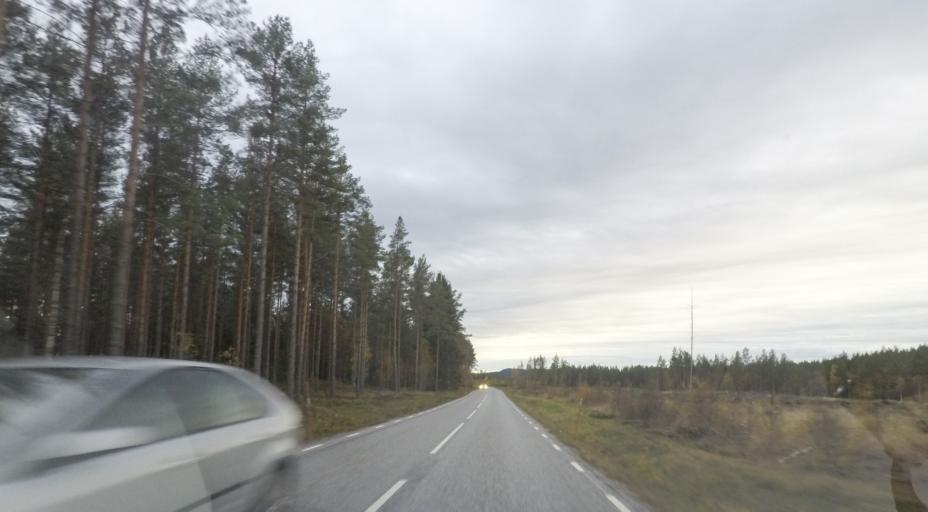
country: SE
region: OErebro
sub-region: Hallefors Kommun
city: Haellefors
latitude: 59.8305
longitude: 14.4967
